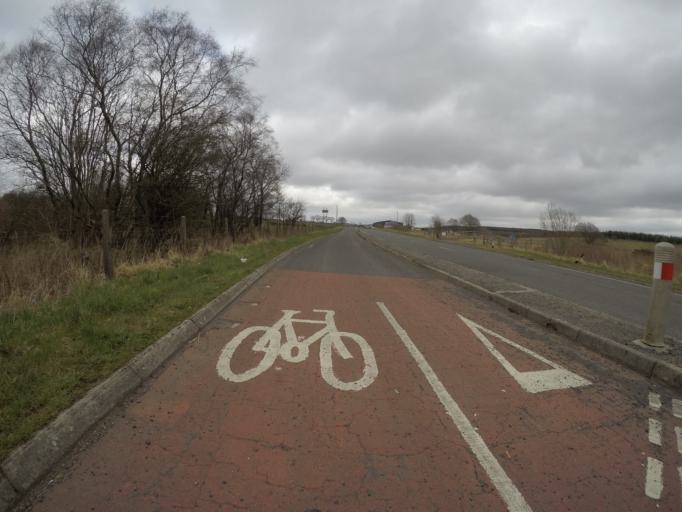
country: GB
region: Scotland
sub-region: East Ayrshire
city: Stewarton
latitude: 55.6734
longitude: -4.4382
